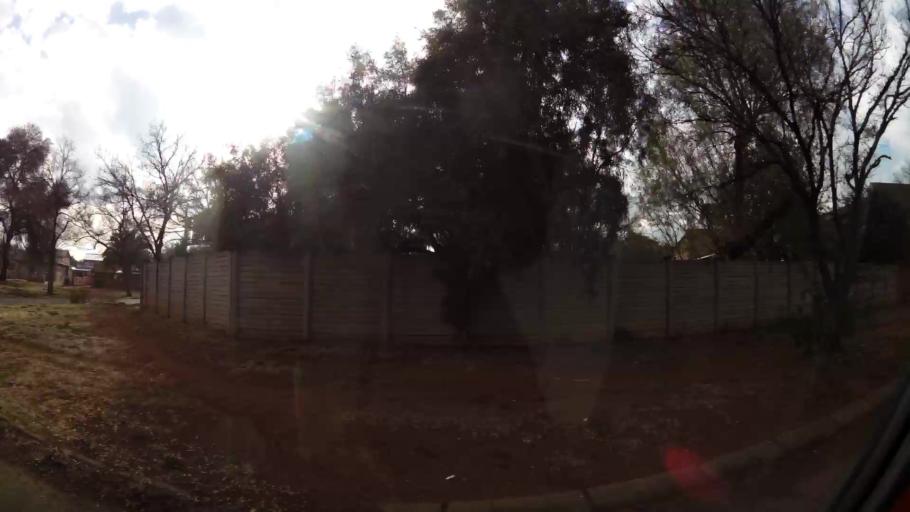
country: ZA
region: Gauteng
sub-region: Sedibeng District Municipality
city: Vanderbijlpark
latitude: -26.6991
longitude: 27.8133
